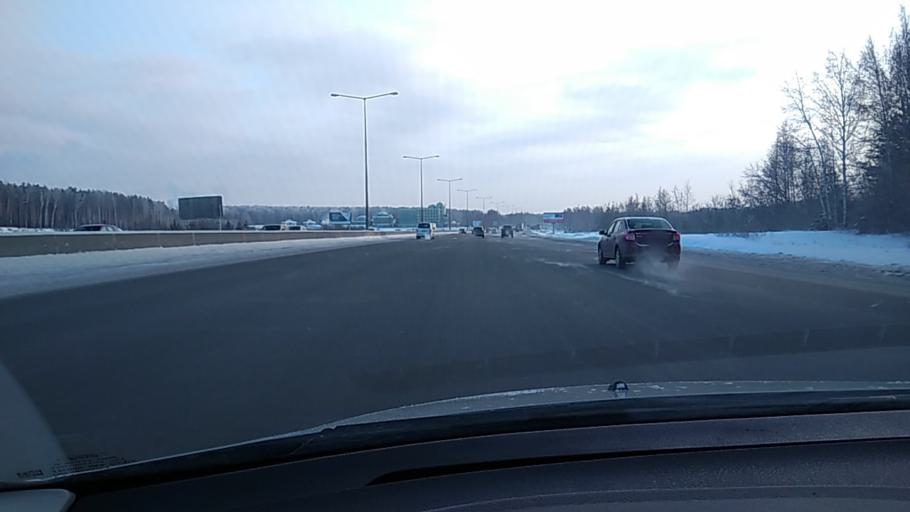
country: RU
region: Sverdlovsk
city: Istok
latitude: 56.7799
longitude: 60.7064
